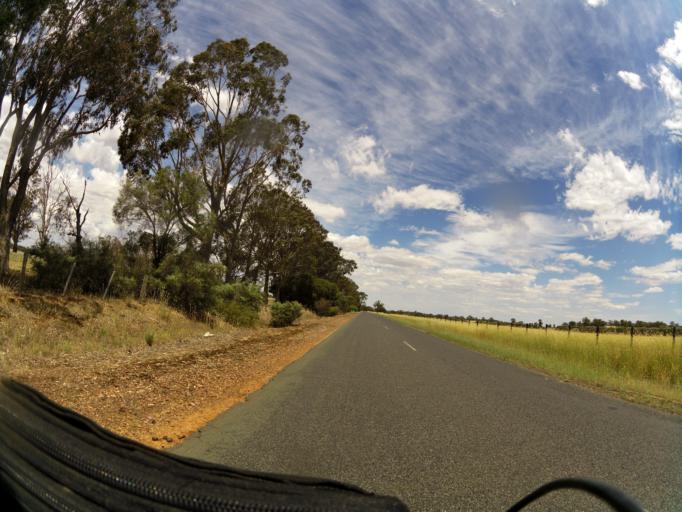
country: AU
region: Victoria
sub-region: Campaspe
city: Kyabram
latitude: -36.7673
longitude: 145.1082
